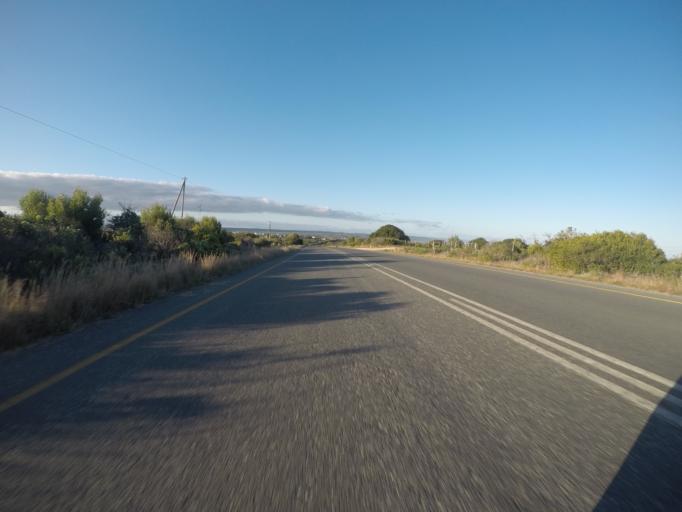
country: ZA
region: Western Cape
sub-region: Eden District Municipality
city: Riversdale
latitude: -34.3924
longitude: 21.3951
